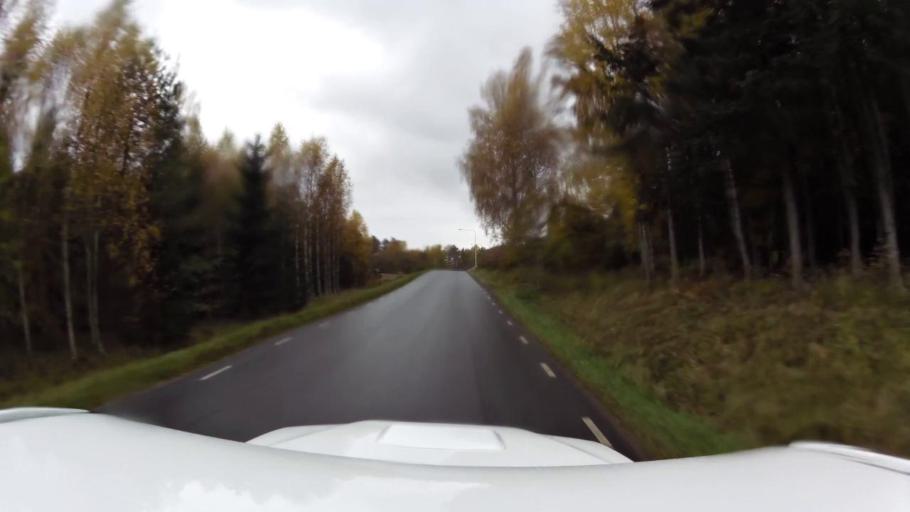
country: SE
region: OEstergoetland
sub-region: Linkopings Kommun
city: Ljungsbro
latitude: 58.5198
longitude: 15.5222
